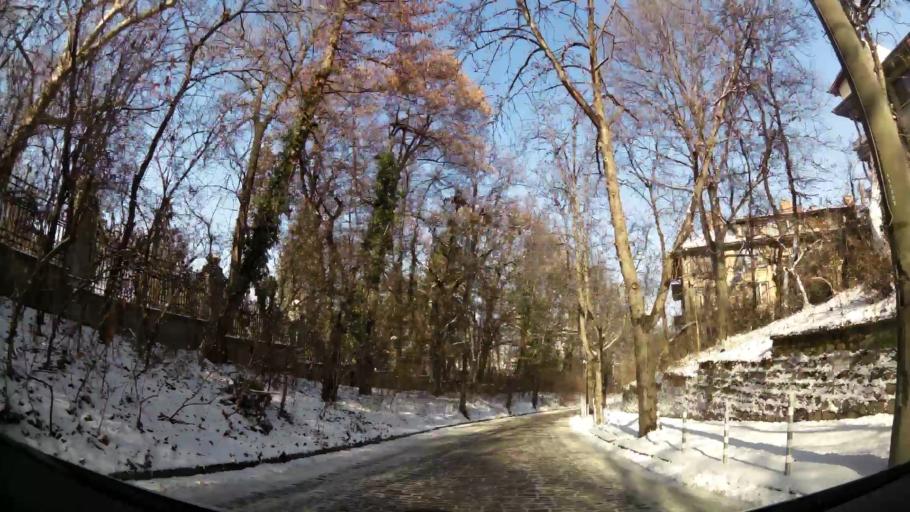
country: BG
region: Sofia-Capital
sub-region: Stolichna Obshtina
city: Sofia
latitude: 42.6762
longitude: 23.3269
